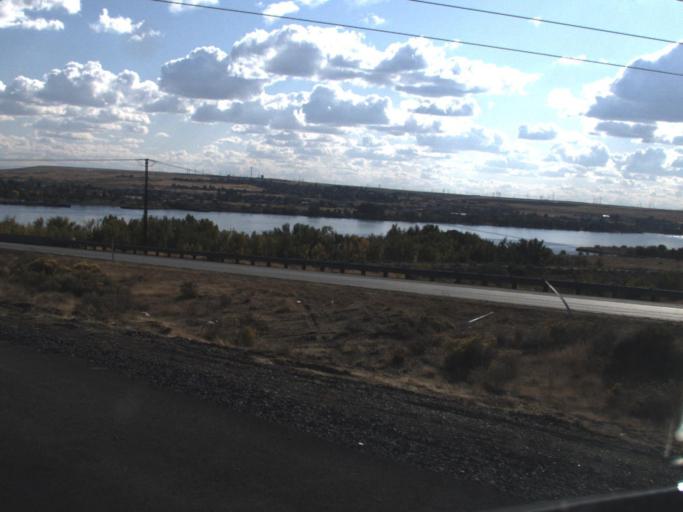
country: US
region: Oregon
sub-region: Umatilla County
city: Umatilla
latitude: 45.9400
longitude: -119.3324
